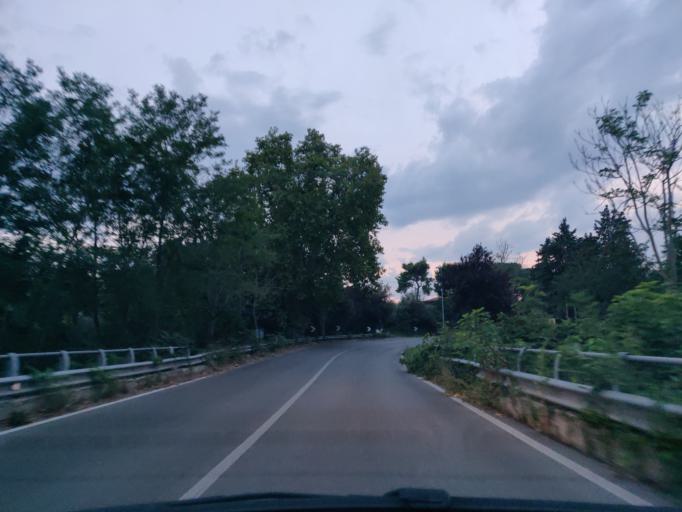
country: IT
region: Latium
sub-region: Provincia di Viterbo
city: San Martino al Cimino
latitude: 42.3827
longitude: 12.0795
